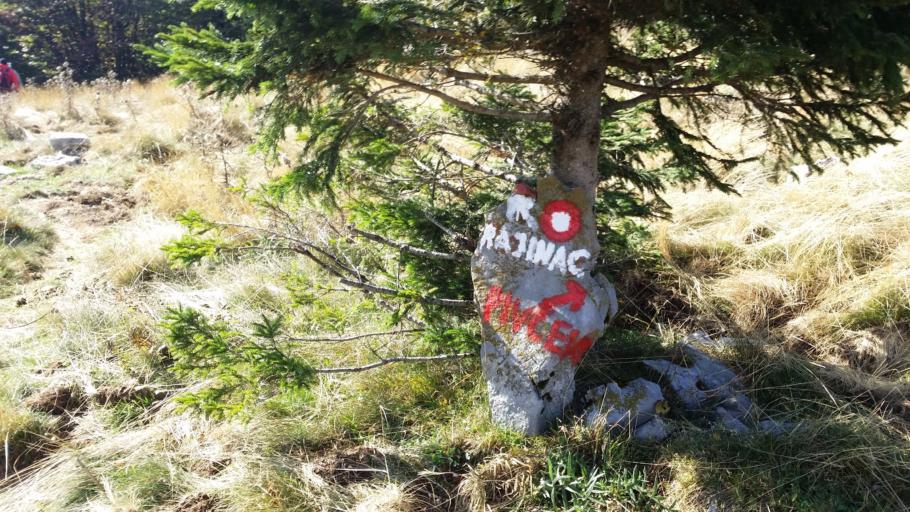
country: HR
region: Licko-Senjska
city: Senj
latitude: 44.8106
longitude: 14.9930
